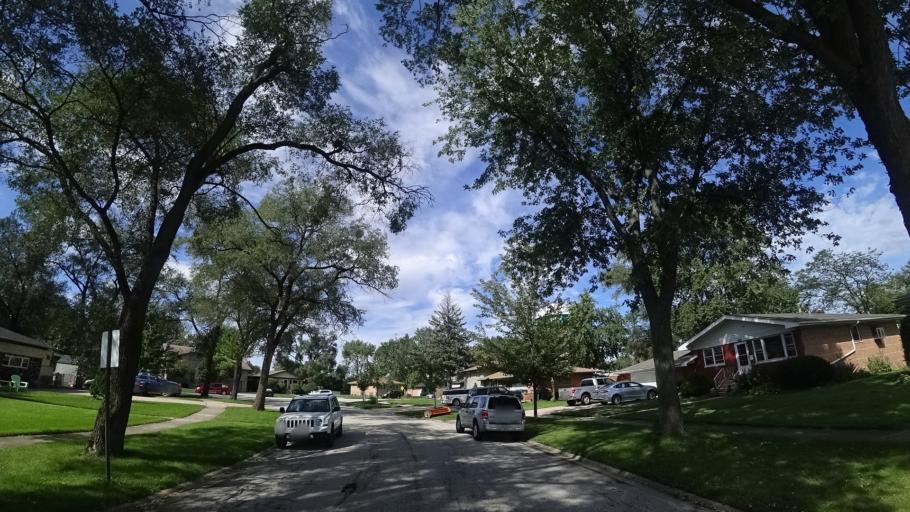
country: US
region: Illinois
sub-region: Cook County
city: Chicago Ridge
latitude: 41.7005
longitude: -87.7822
